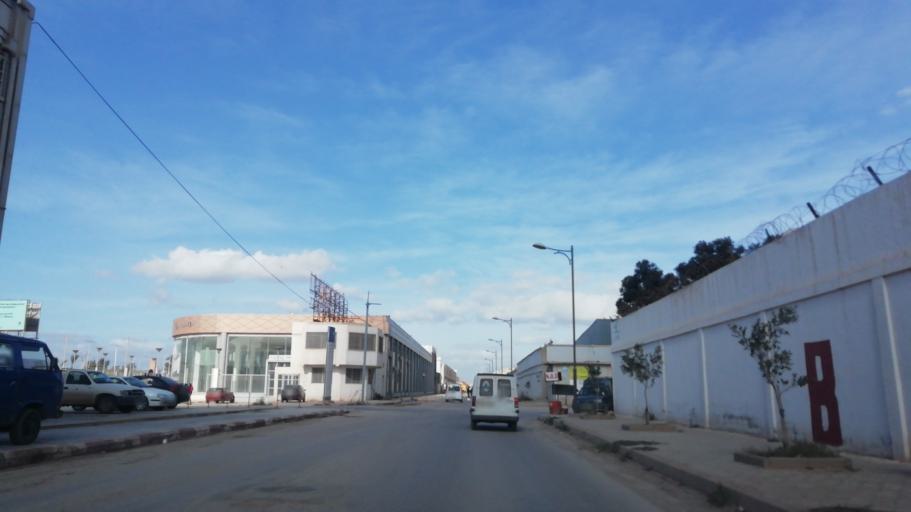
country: DZ
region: Oran
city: Es Senia
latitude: 35.6445
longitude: -0.5888
